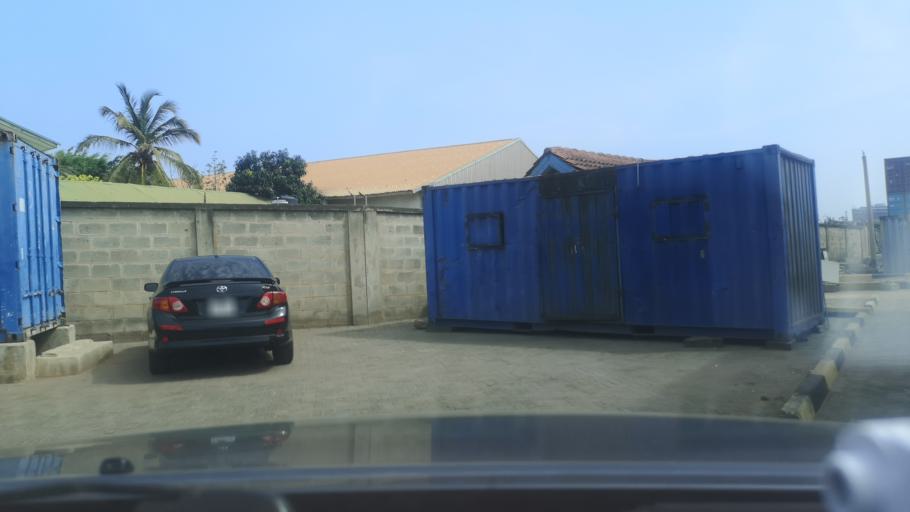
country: GH
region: Greater Accra
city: Tema
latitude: 5.6270
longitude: 0.0009
